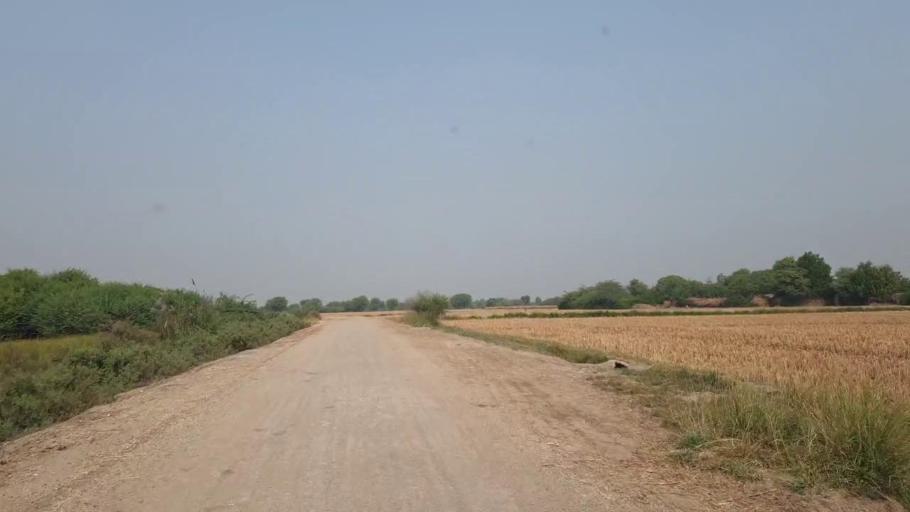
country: PK
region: Sindh
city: Matli
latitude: 25.1613
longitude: 68.7294
